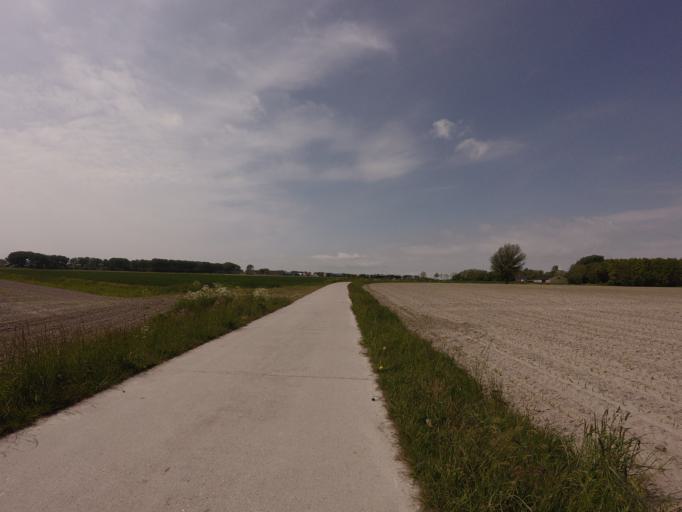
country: NL
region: Friesland
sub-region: Sudwest Fryslan
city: Bolsward
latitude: 53.1074
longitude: 5.4832
